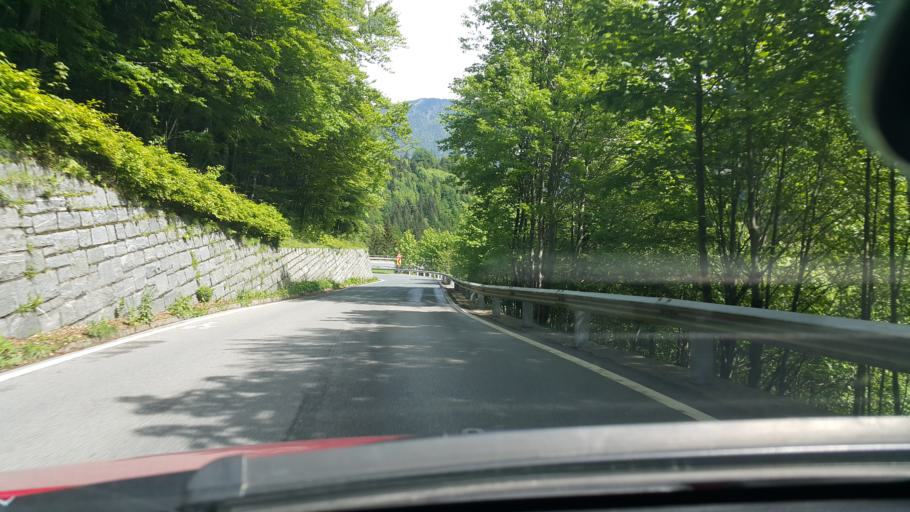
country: AT
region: Carinthia
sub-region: Politischer Bezirk Klagenfurt Land
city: Ferlach
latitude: 46.4506
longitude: 14.2555
